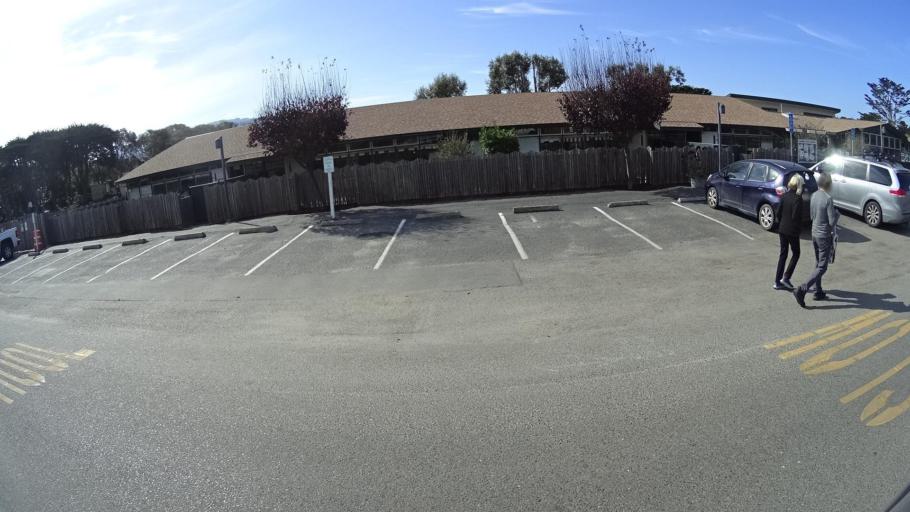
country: US
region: California
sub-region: Monterey County
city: Carmel-by-the-Sea
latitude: 36.5427
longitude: -121.9242
